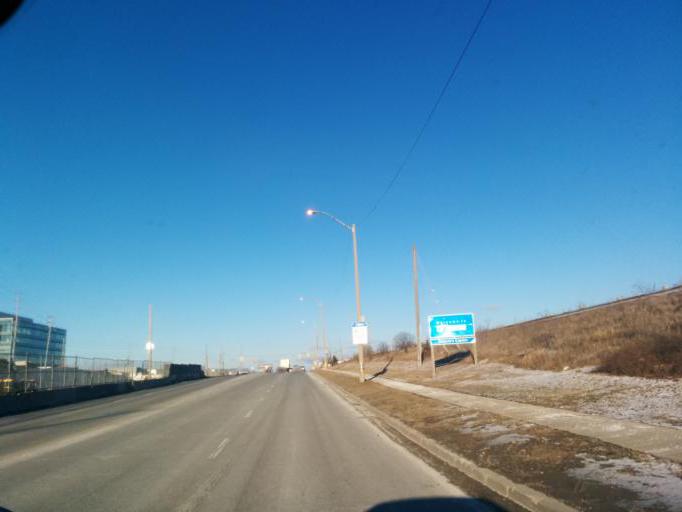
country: CA
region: Ontario
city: Etobicoke
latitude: 43.6470
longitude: -79.6080
